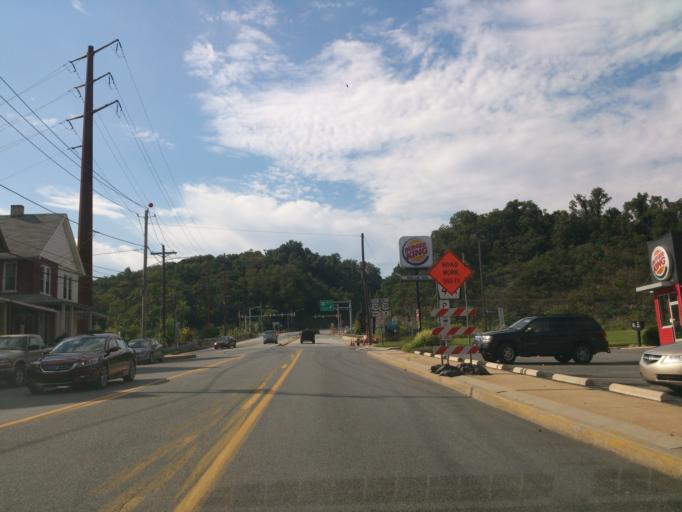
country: US
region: Pennsylvania
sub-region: Lancaster County
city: Columbia
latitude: 40.0375
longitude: -76.5089
